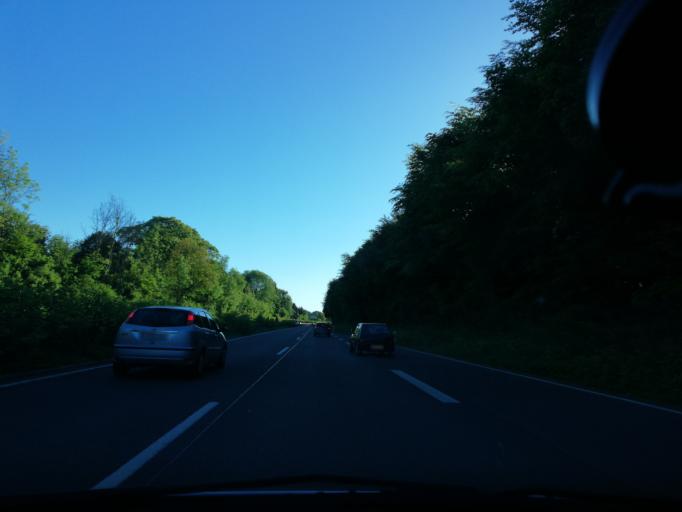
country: DE
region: North Rhine-Westphalia
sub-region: Regierungsbezirk Dusseldorf
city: Wuppertal
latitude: 51.2406
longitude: 7.1707
